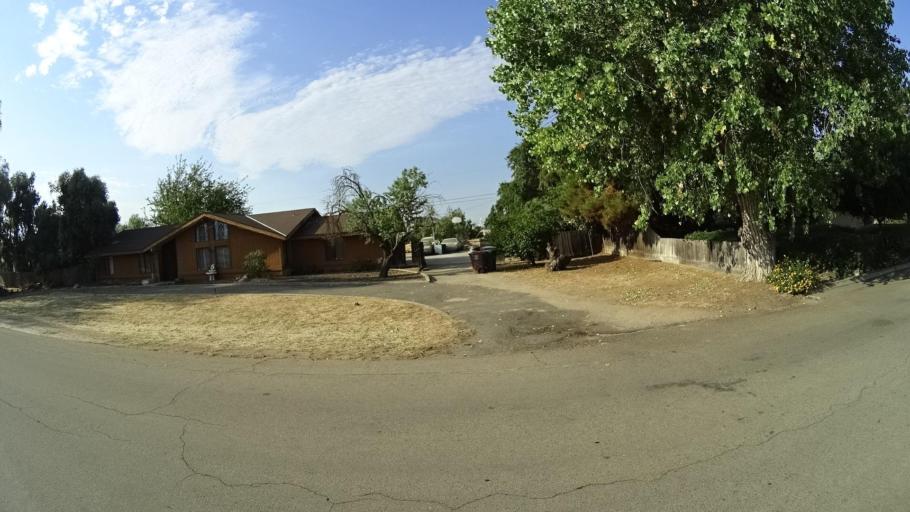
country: US
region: California
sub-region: Fresno County
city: Sunnyside
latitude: 36.7095
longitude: -119.6943
